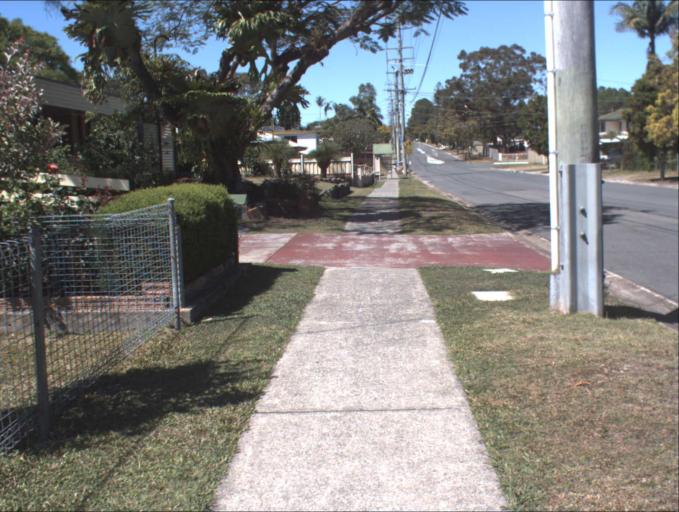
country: AU
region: Queensland
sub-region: Logan
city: Logan City
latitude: -27.6340
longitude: 153.1257
